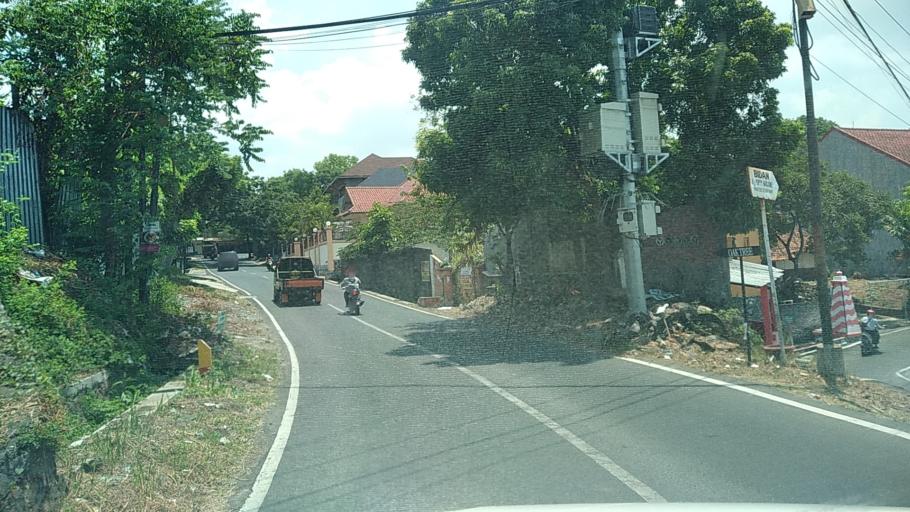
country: ID
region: Central Java
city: Semarang
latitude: -7.0130
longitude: 110.4130
